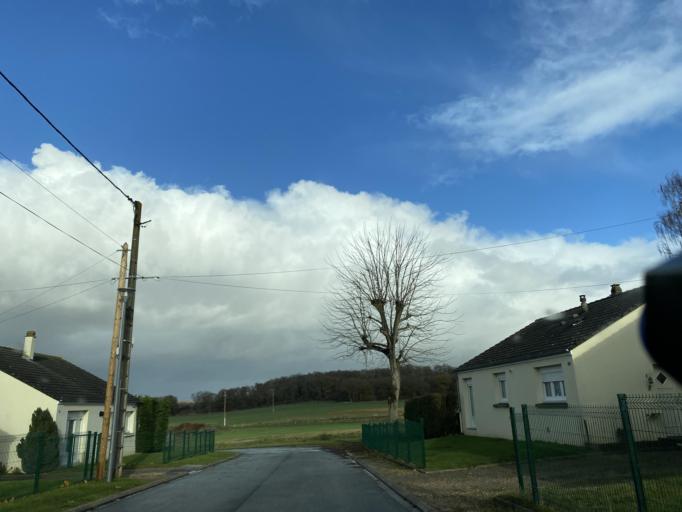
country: FR
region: Centre
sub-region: Departement d'Eure-et-Loir
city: Brezolles
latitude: 48.6946
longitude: 1.0761
